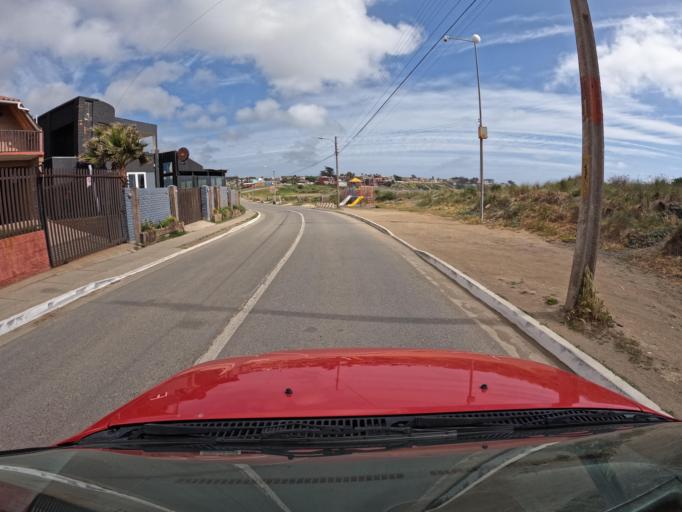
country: CL
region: O'Higgins
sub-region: Provincia de Colchagua
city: Santa Cruz
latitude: -34.3861
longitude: -72.0176
